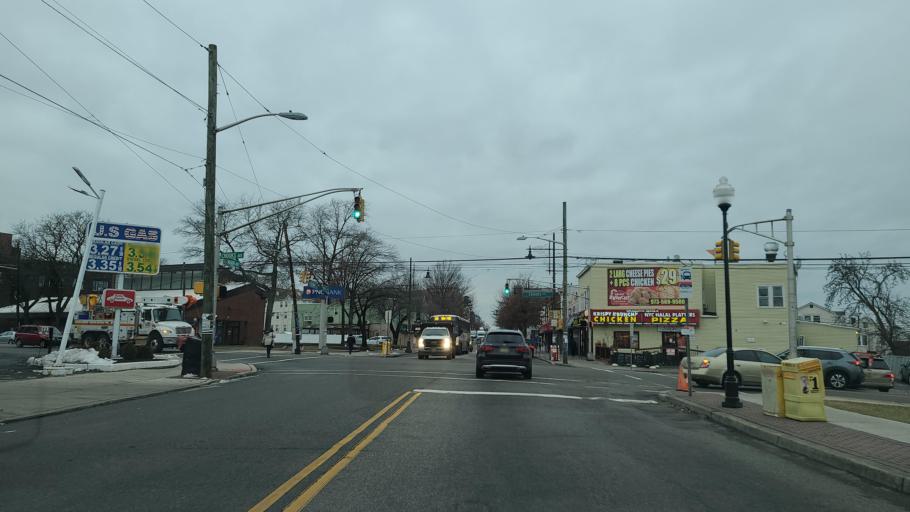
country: US
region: New Jersey
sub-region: Passaic County
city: Clifton
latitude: 40.8894
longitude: -74.1542
